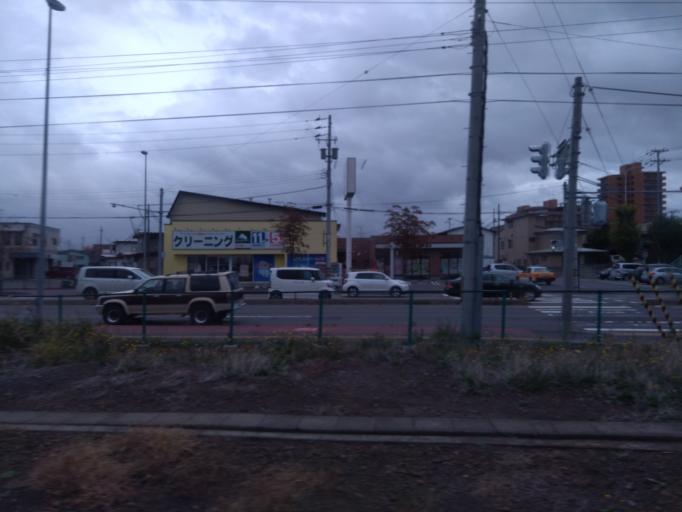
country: JP
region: Hokkaido
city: Hakodate
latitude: 41.8011
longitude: 140.7341
